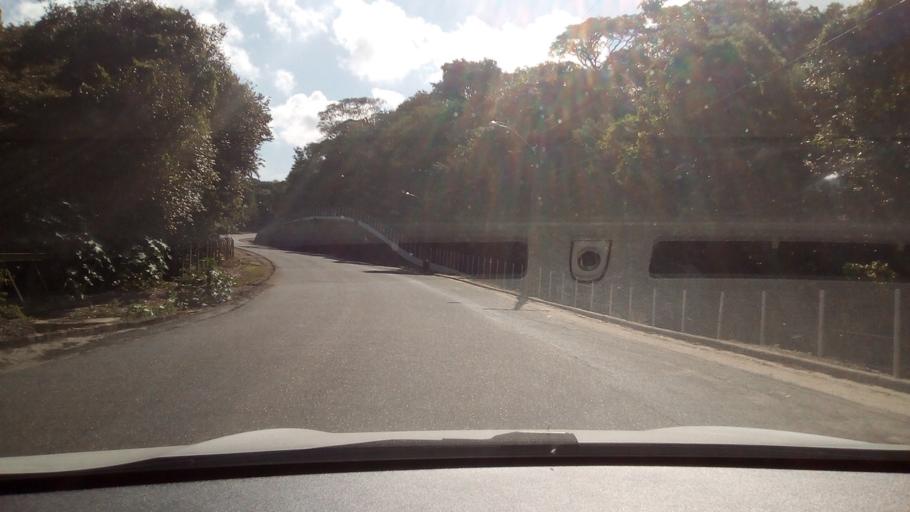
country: BR
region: Paraiba
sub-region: Joao Pessoa
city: Joao Pessoa
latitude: -7.1381
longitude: -34.8416
